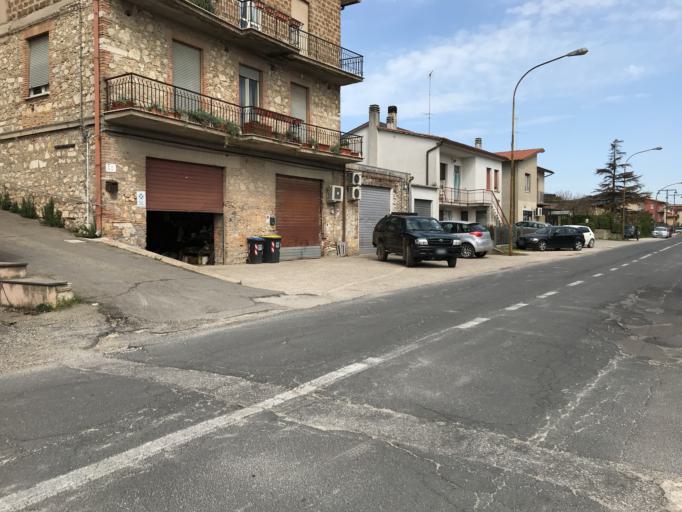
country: IT
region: Umbria
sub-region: Provincia di Terni
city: Amelia
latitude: 42.5458
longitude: 12.4184
